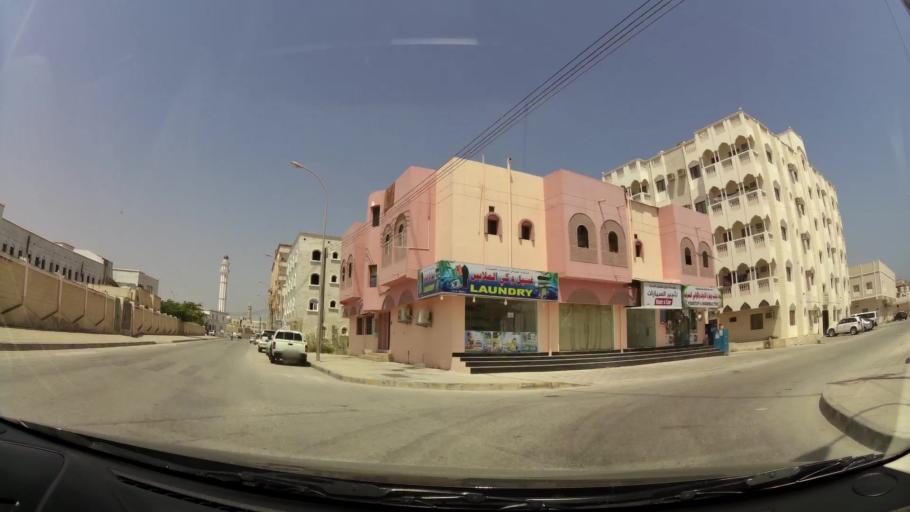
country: OM
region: Zufar
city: Salalah
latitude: 17.0149
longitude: 54.0871
